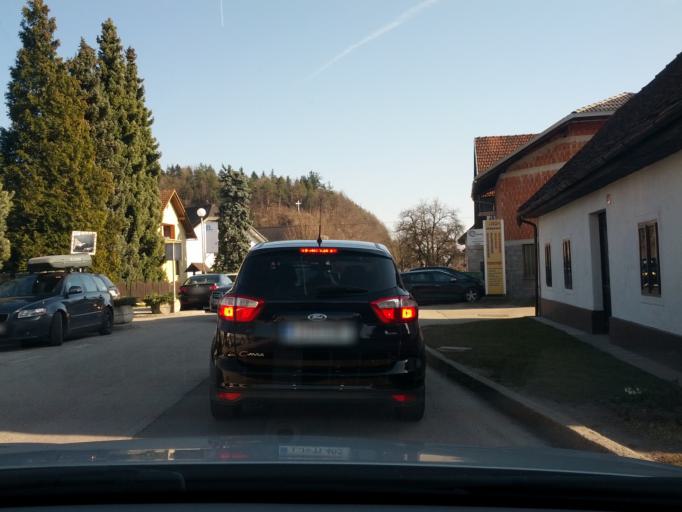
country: SI
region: Naklo
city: Naklo
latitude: 46.2734
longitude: 14.3176
